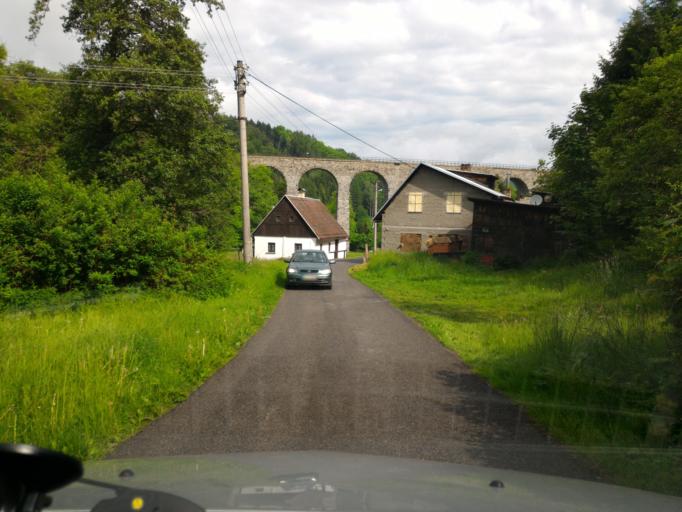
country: CZ
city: Osecna
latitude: 50.7568
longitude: 14.9412
